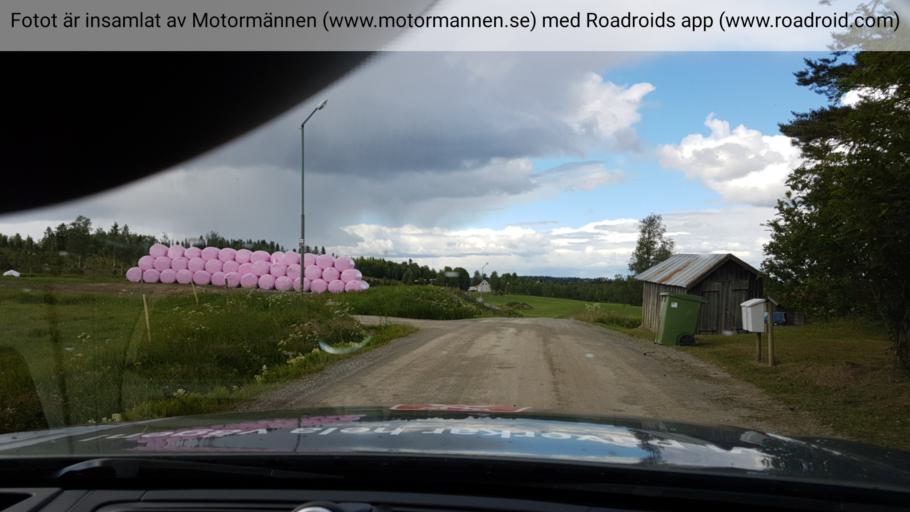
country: SE
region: Jaemtland
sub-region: Bergs Kommun
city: Hoverberg
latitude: 62.9401
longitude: 14.2718
